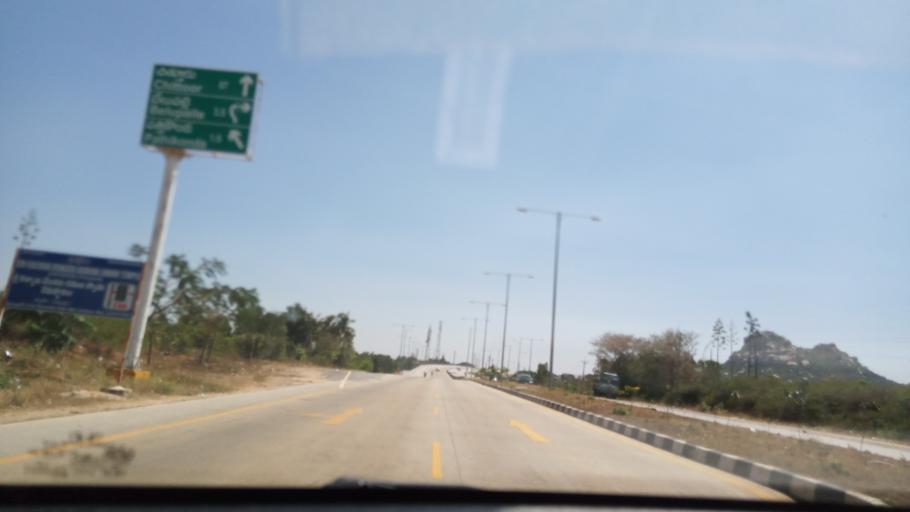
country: IN
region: Andhra Pradesh
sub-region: Chittoor
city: Palmaner
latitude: 13.1815
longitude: 78.6296
